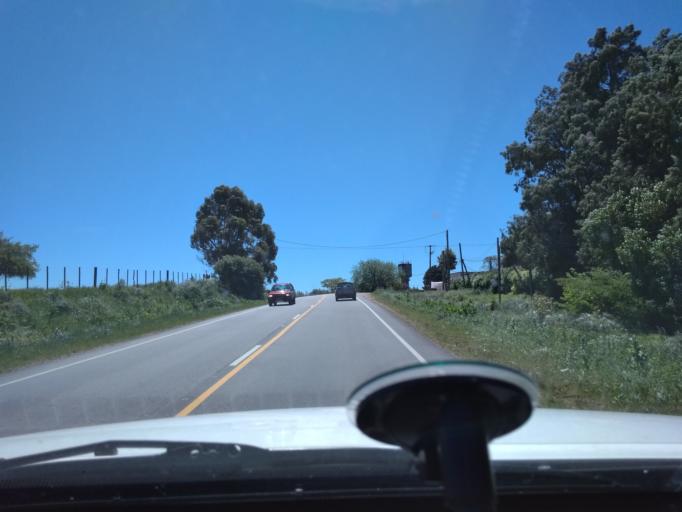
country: UY
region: Canelones
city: Las Piedras
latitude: -34.7114
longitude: -56.2907
